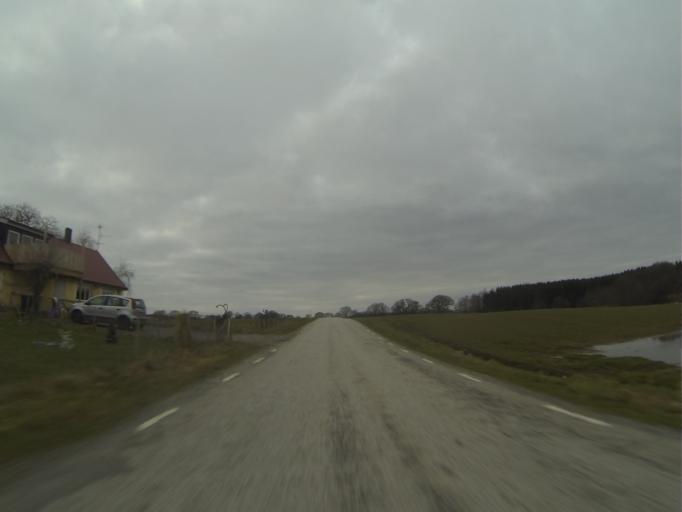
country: SE
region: Skane
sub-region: Skurups Kommun
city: Skurup
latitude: 55.5269
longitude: 13.4418
